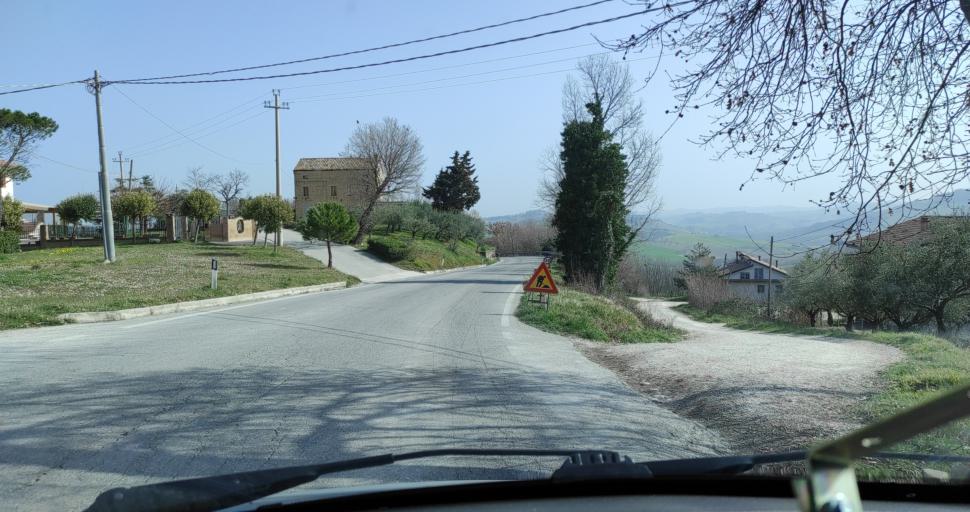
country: IT
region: The Marches
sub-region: Provincia di Macerata
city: Loro Piceno
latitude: 43.1727
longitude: 13.4273
